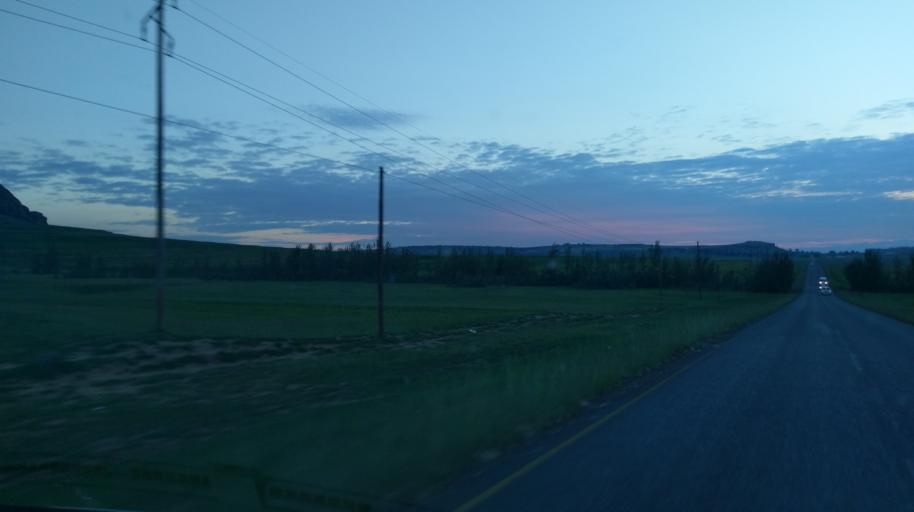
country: ZA
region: Orange Free State
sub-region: Thabo Mofutsanyana District Municipality
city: Ficksburg
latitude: -28.9484
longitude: 27.8128
